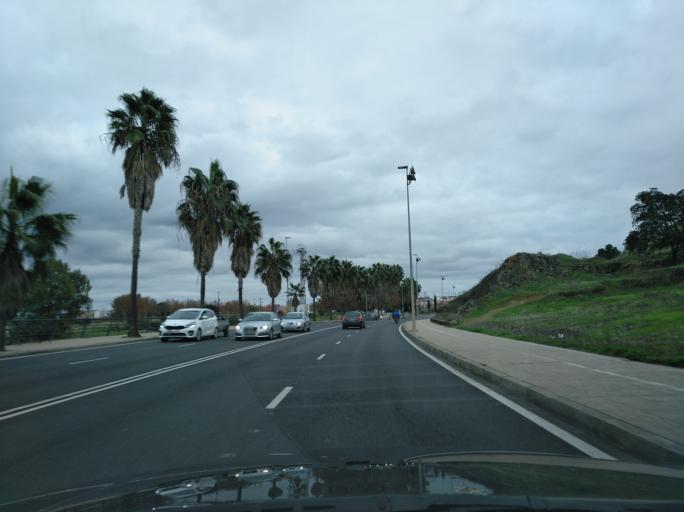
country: ES
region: Extremadura
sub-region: Provincia de Badajoz
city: Badajoz
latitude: 38.8844
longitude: -6.9671
